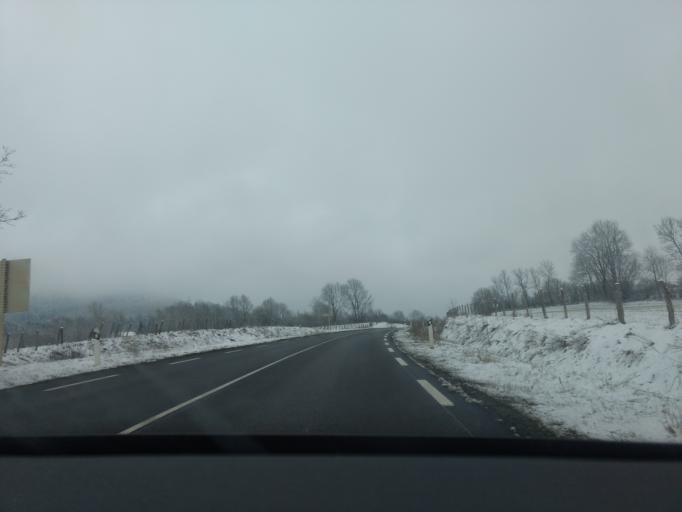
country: FR
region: Franche-Comte
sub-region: Departement du Jura
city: Champagnole
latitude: 46.7742
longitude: 5.9053
